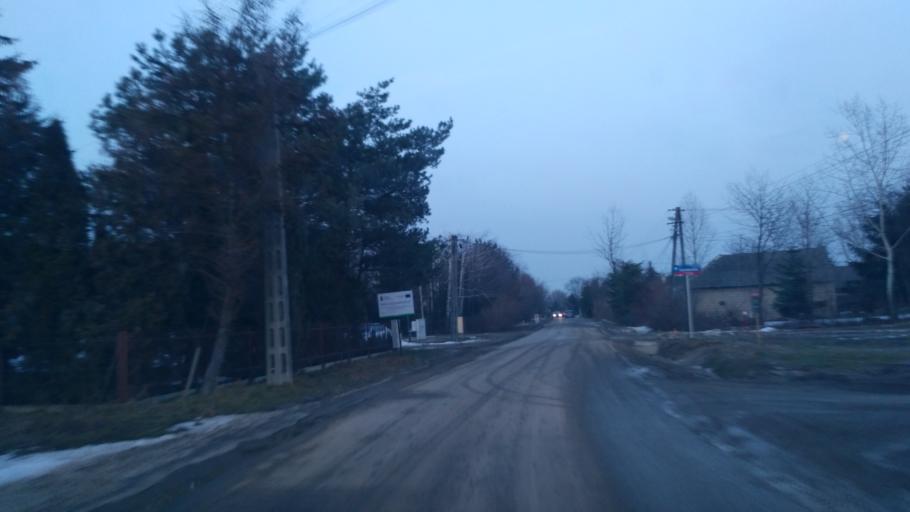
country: PL
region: Subcarpathian Voivodeship
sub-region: Powiat rzeszowski
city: Boguchwala
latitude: 49.9896
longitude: 21.9759
